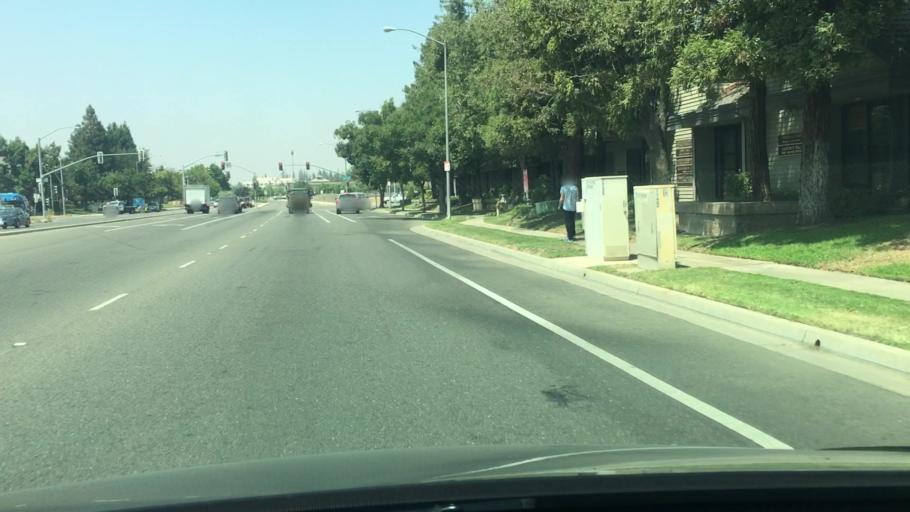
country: US
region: California
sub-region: Fresno County
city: Clovis
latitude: 36.8508
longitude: -119.7837
